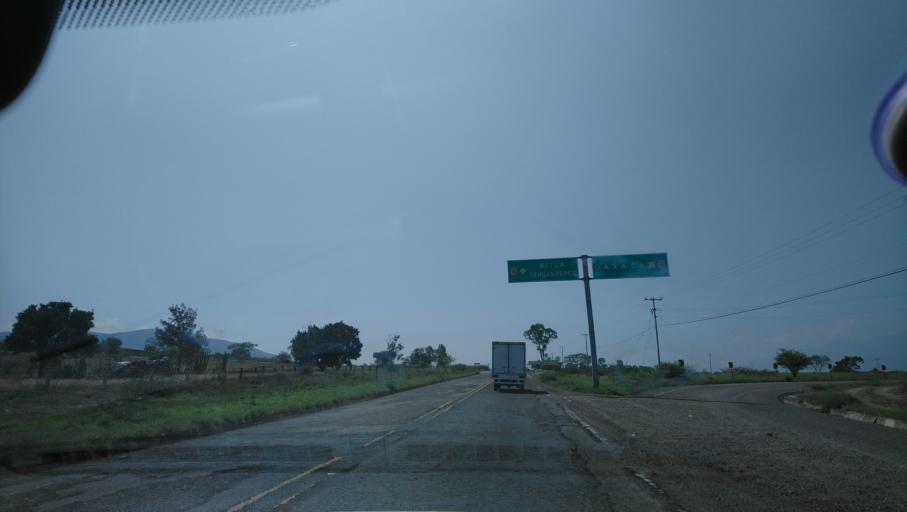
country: MX
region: Oaxaca
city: Santa Maria del Tule
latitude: 17.0389
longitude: -96.6205
